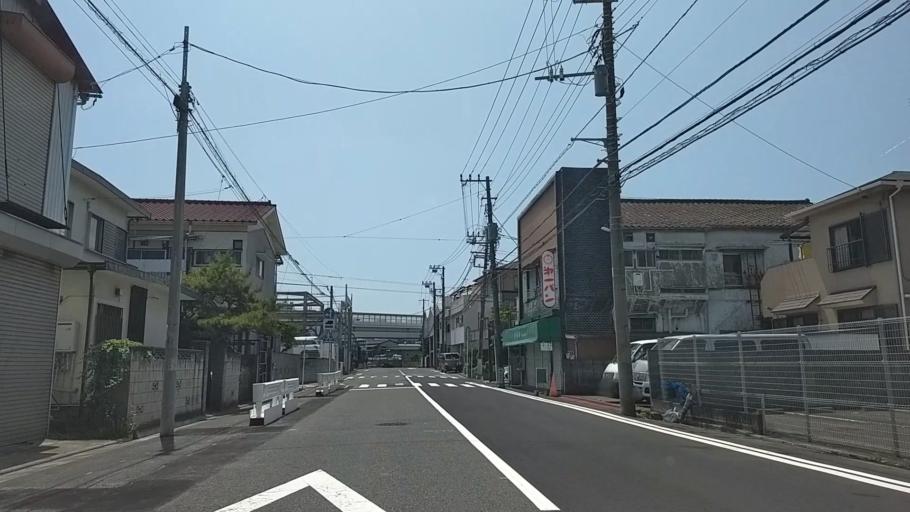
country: JP
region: Kanagawa
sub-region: Kawasaki-shi
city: Kawasaki
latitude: 35.5040
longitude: 139.6987
